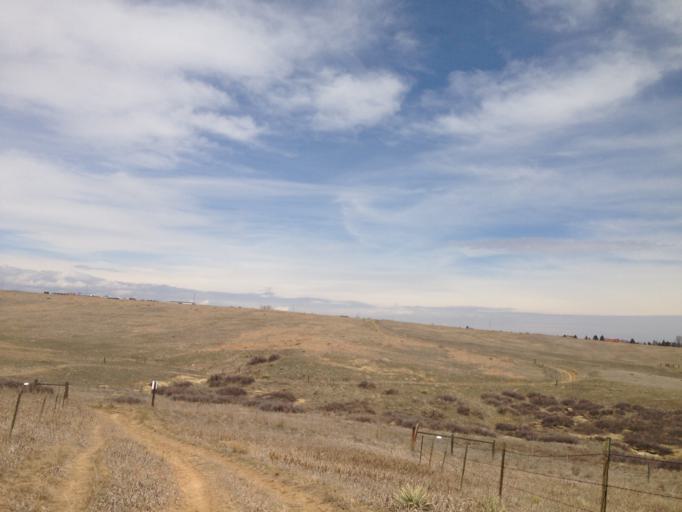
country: US
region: Colorado
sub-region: Boulder County
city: Gunbarrel
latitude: 40.0578
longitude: -105.1406
